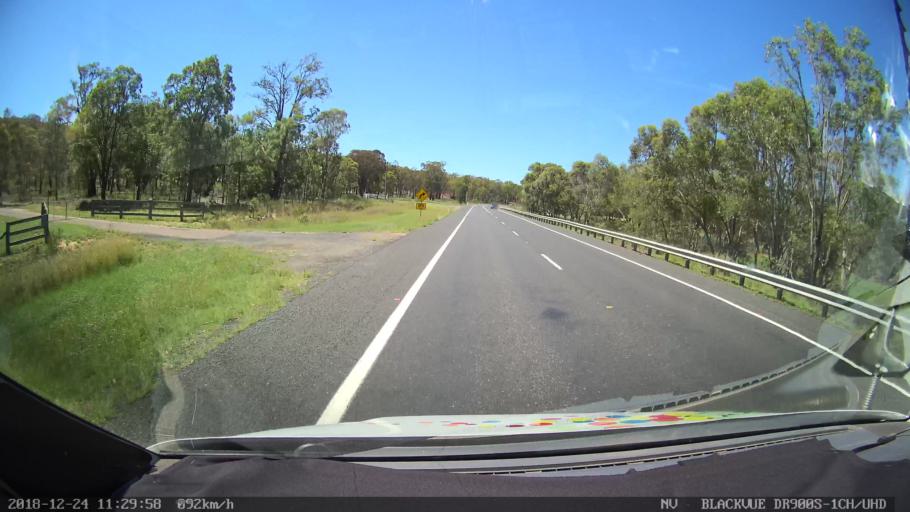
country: AU
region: New South Wales
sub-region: Upper Hunter Shire
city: Merriwa
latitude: -32.1990
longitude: 150.4663
